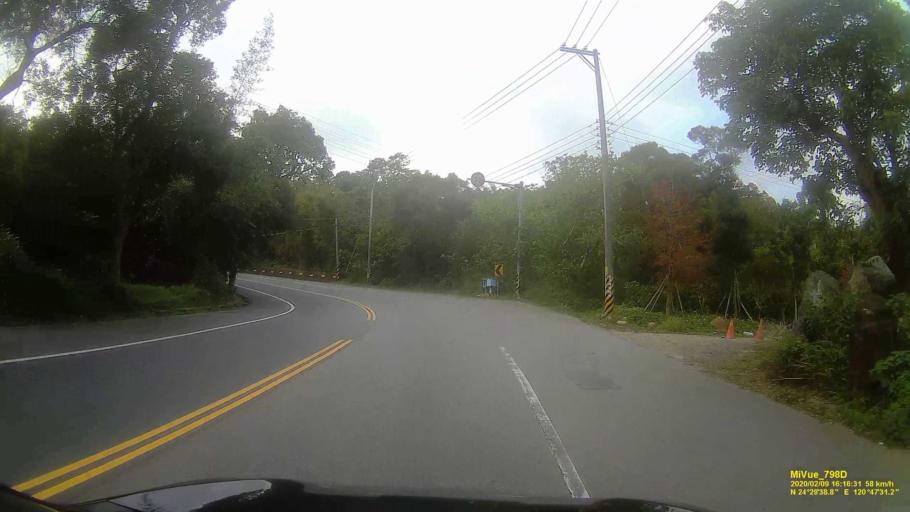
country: TW
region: Taiwan
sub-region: Miaoli
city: Miaoli
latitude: 24.4944
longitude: 120.7917
